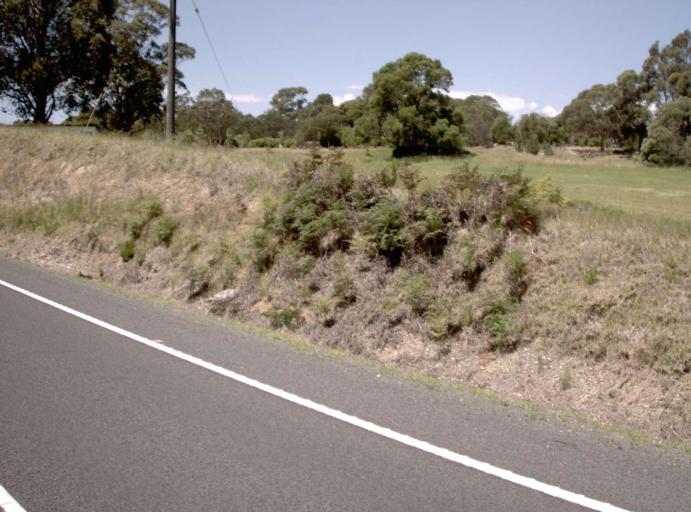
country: AU
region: Victoria
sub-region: East Gippsland
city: Lakes Entrance
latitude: -37.6997
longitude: 148.7182
